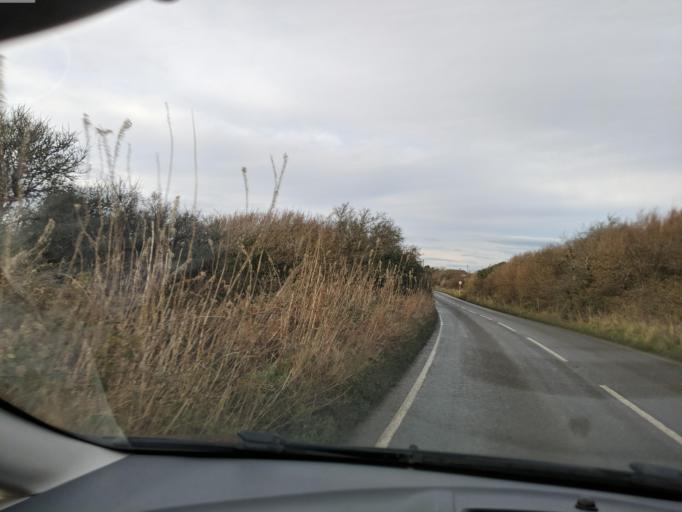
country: GB
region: England
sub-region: Cornwall
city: Jacobstow
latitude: 50.6925
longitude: -4.6160
